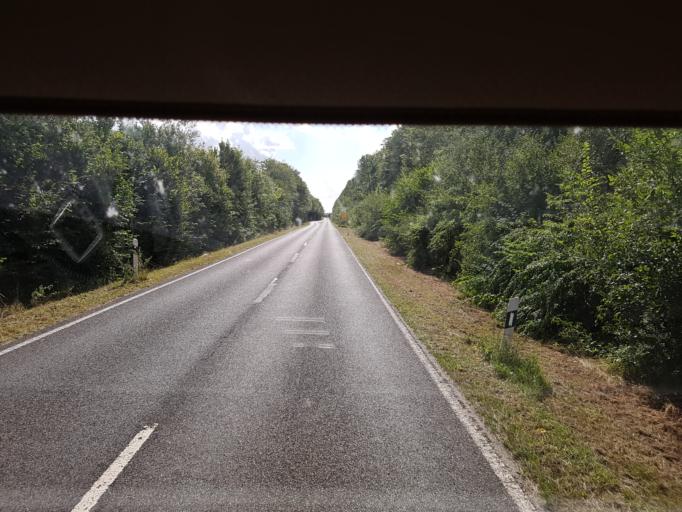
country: DE
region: Rheinland-Pfalz
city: Bekond
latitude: 49.8654
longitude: 6.7836
